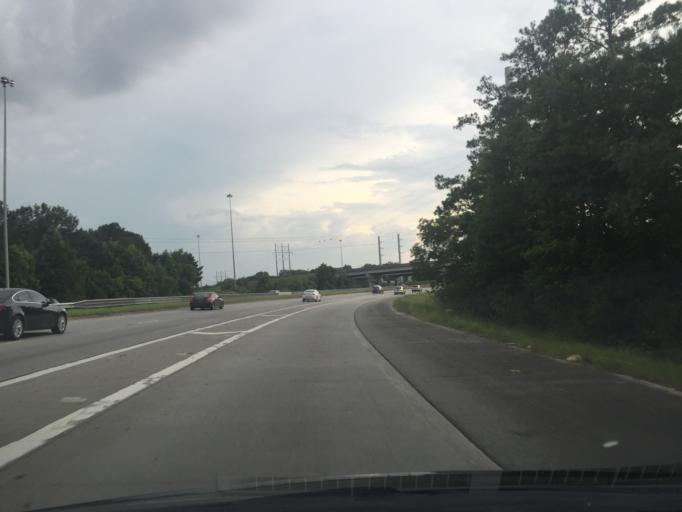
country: US
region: Georgia
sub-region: Chatham County
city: Savannah
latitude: 32.0402
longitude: -81.1446
